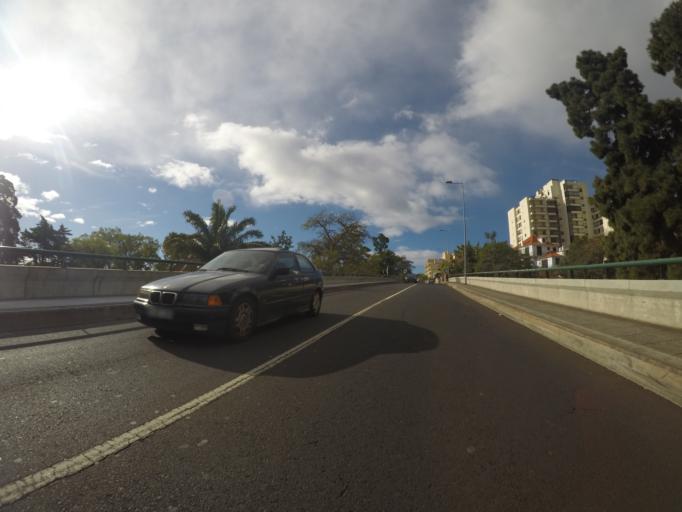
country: PT
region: Madeira
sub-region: Funchal
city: Funchal
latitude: 32.6452
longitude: -16.9248
